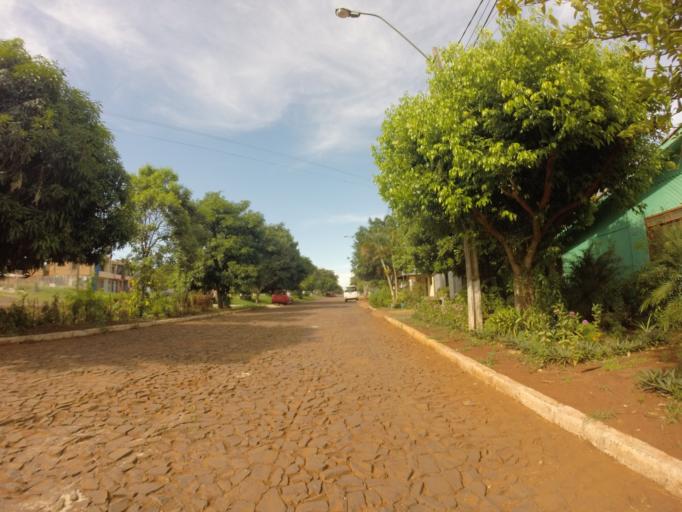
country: PY
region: Alto Parana
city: Ciudad del Este
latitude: -25.3917
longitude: -54.6446
